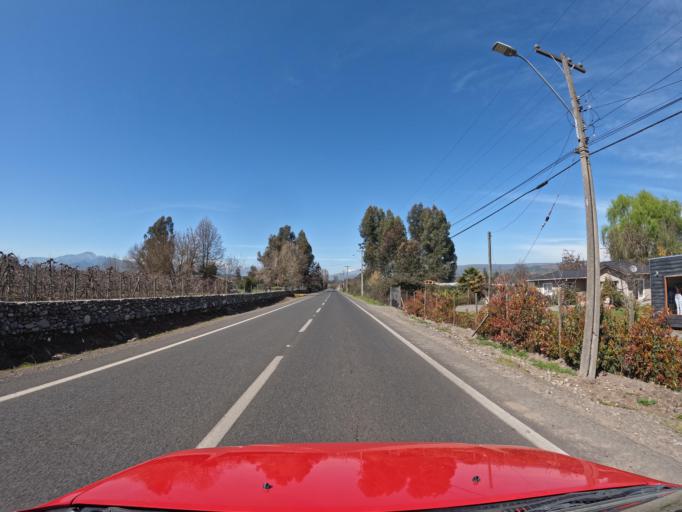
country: CL
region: Maule
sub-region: Provincia de Curico
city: Teno
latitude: -34.9686
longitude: -71.0262
